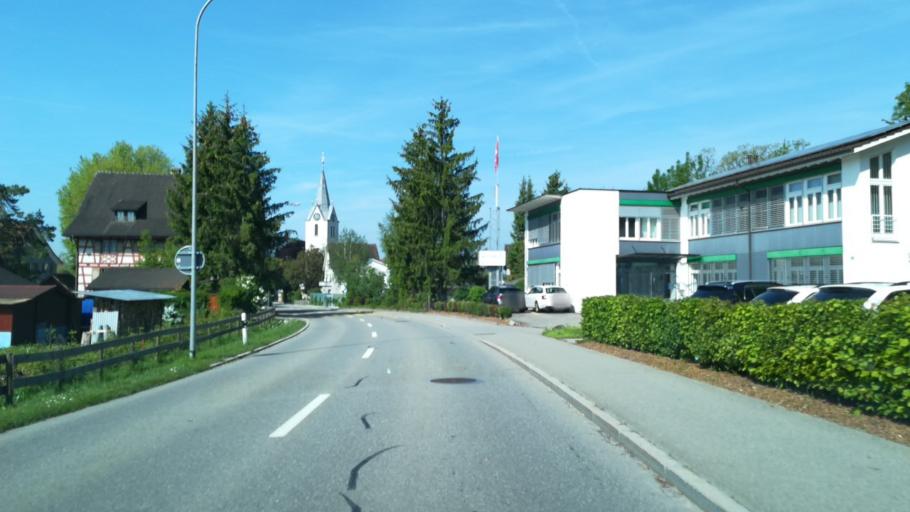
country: CH
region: Thurgau
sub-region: Frauenfeld District
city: Mullheim
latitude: 47.6054
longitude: 9.0118
